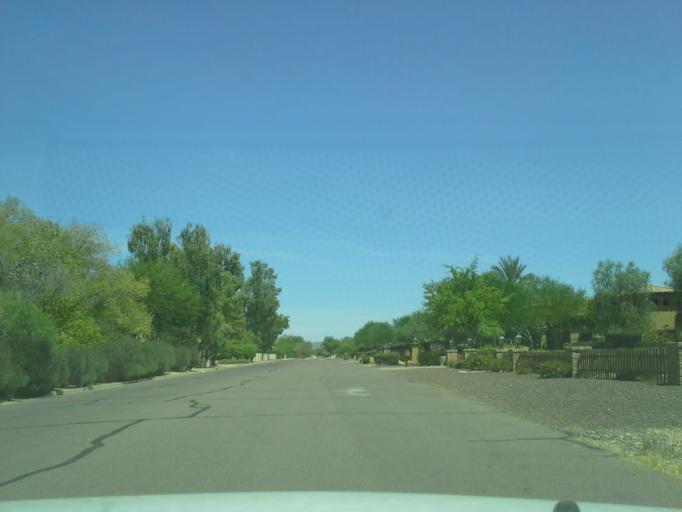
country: US
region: Arizona
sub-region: Maricopa County
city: Scottsdale
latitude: 33.5897
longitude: -111.8677
